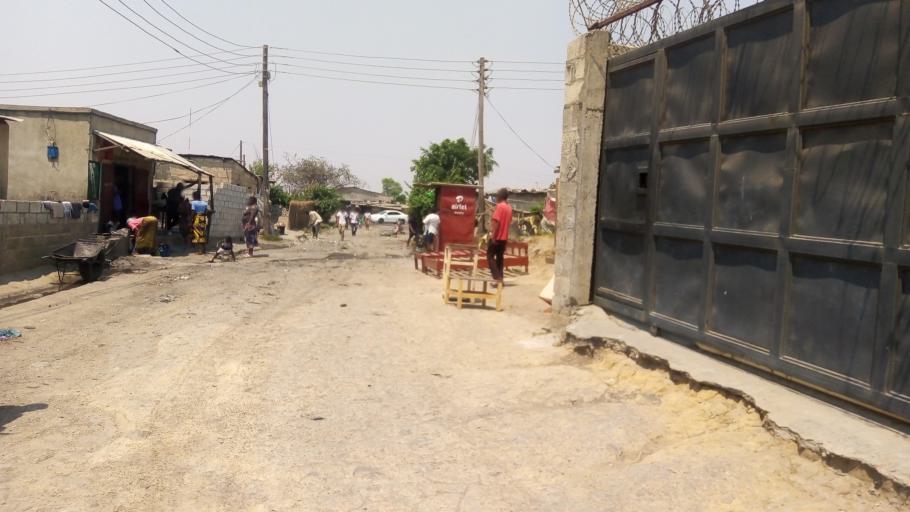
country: ZM
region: Lusaka
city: Lusaka
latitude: -15.4442
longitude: 28.3784
